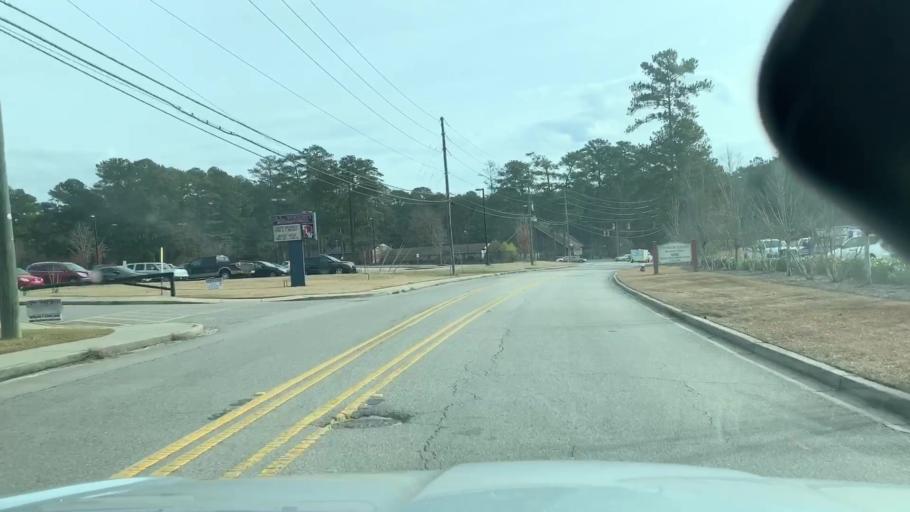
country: US
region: South Carolina
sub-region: Richland County
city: Woodfield
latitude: 34.0821
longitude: -80.9261
